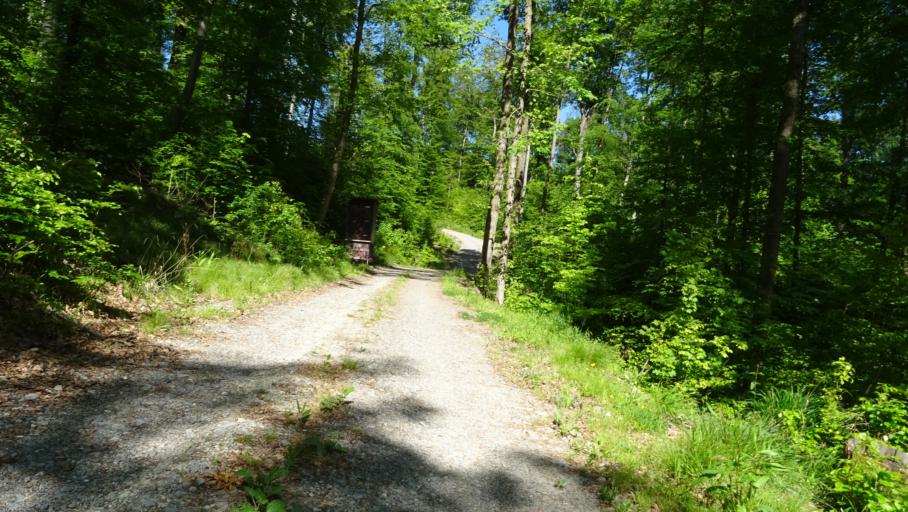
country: DE
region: Baden-Wuerttemberg
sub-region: Karlsruhe Region
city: Obrigheim
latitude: 49.3712
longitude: 9.1079
